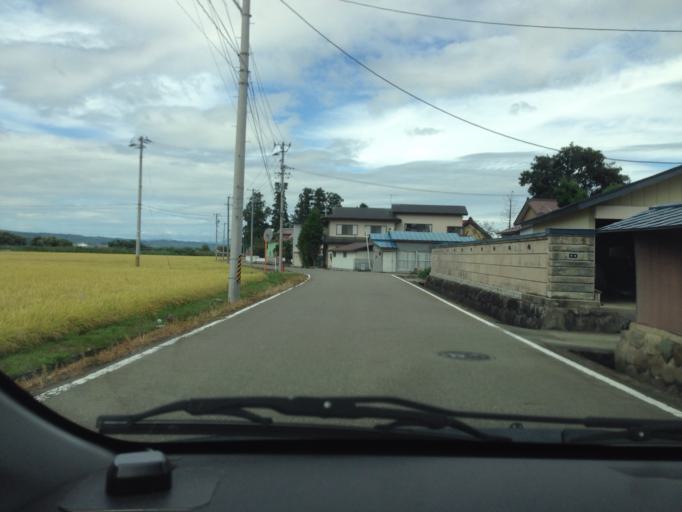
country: JP
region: Fukushima
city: Kitakata
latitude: 37.4833
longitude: 139.8560
